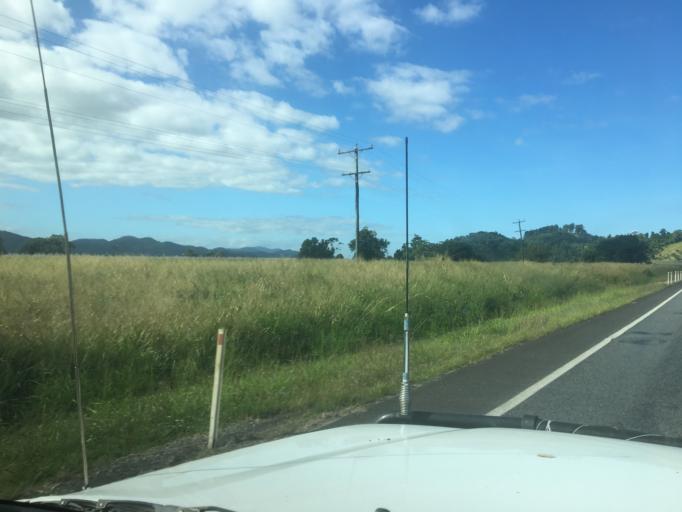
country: AU
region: Queensland
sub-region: Cassowary Coast
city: Innisfail
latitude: -17.2803
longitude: 145.9214
